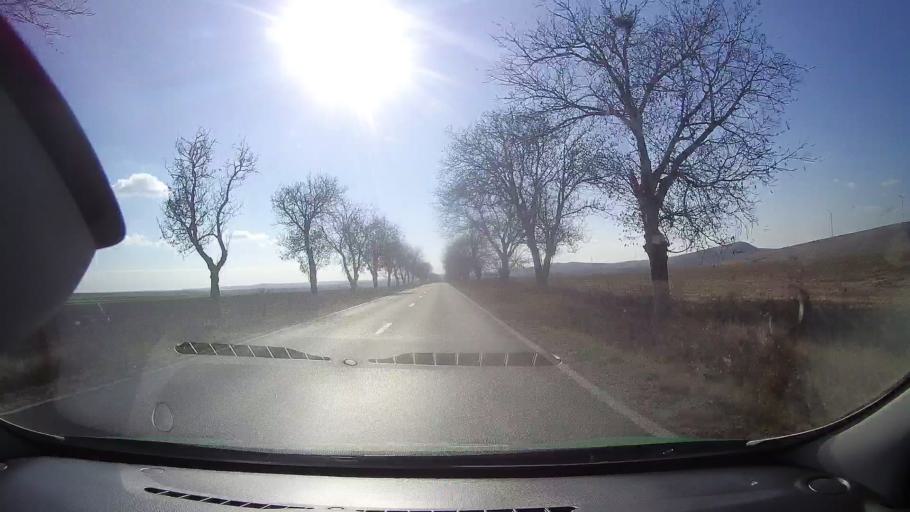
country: RO
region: Tulcea
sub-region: Comuna Ceamurlia de Jos
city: Ceamurlia de Jos
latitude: 44.7890
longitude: 28.6897
